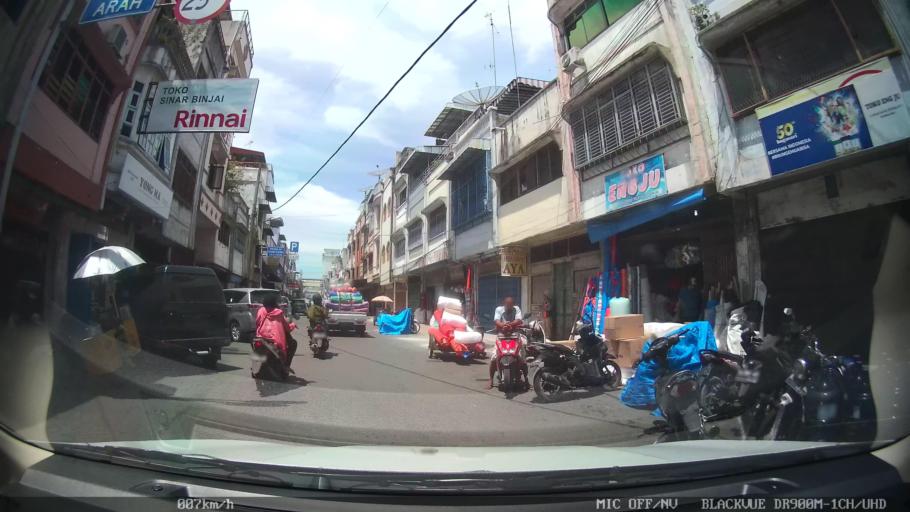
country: ID
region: North Sumatra
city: Binjai
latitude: 3.6091
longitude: 98.4915
